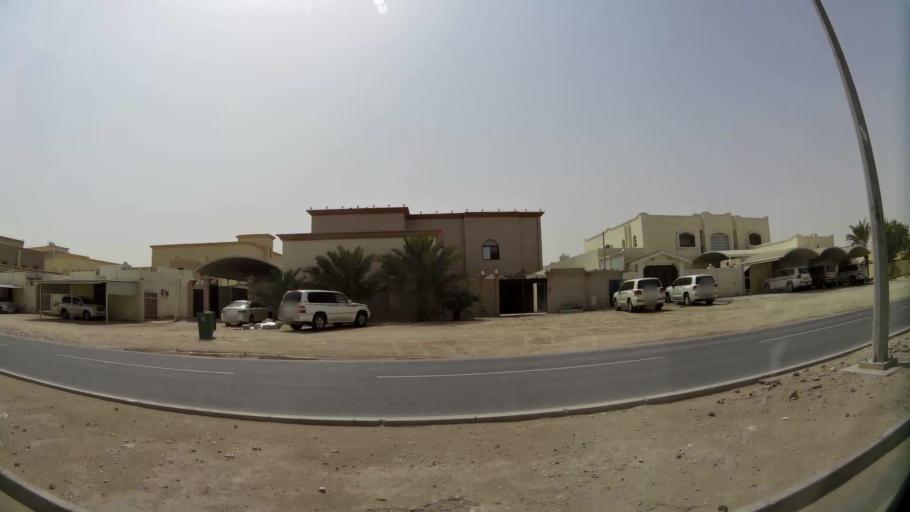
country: QA
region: Baladiyat ar Rayyan
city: Ar Rayyan
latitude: 25.2456
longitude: 51.3782
